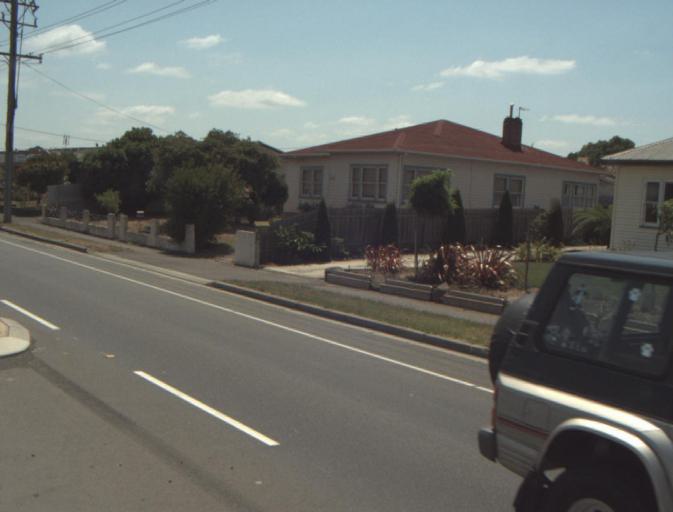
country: AU
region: Tasmania
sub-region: Launceston
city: Summerhill
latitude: -41.4872
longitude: 147.1677
